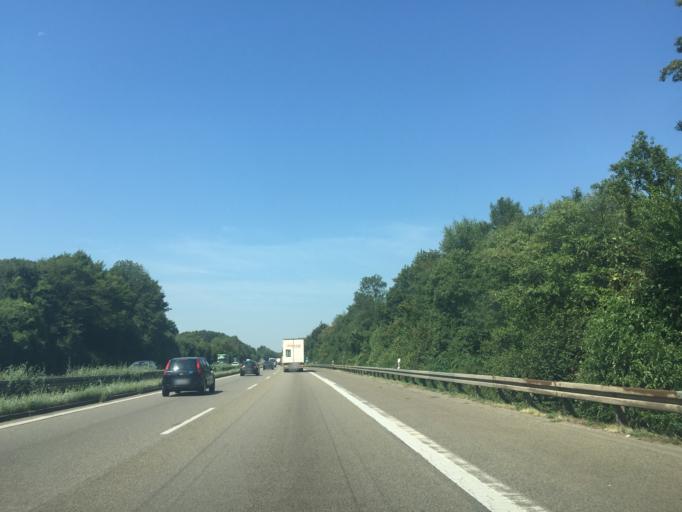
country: DE
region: Baden-Wuerttemberg
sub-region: Karlsruhe Region
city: Zuzenhausen
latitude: 49.2572
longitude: 8.8321
